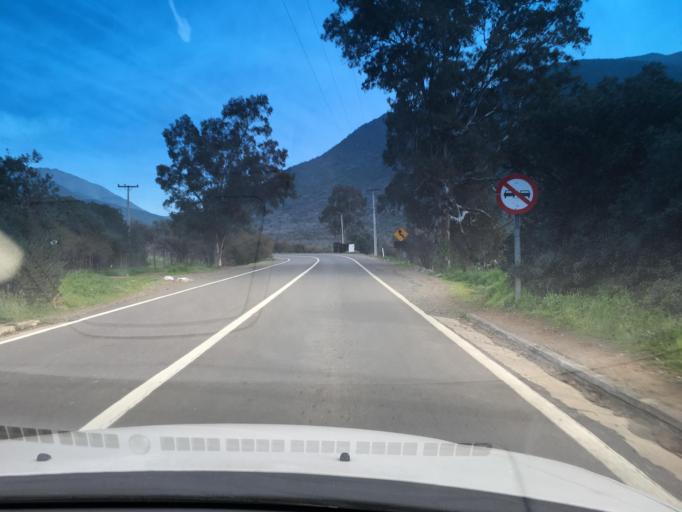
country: CL
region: Santiago Metropolitan
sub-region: Provincia de Chacabuco
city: Lampa
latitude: -33.0750
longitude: -70.9333
